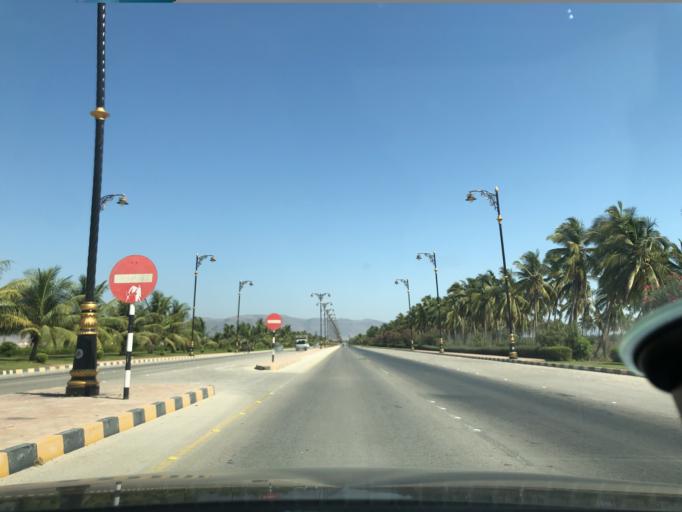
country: OM
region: Zufar
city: Salalah
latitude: 17.0335
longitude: 54.1915
